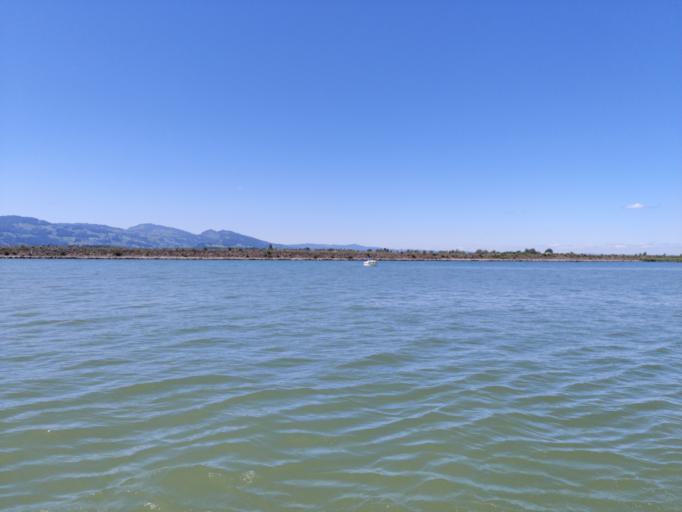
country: AT
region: Vorarlberg
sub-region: Politischer Bezirk Bregenz
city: Hard
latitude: 47.5097
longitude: 9.6697
